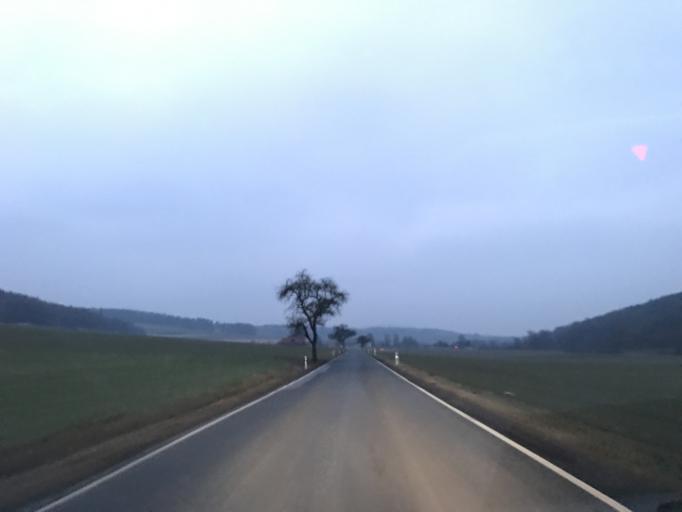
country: DE
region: Hesse
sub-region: Regierungsbezirk Kassel
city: Hofgeismar
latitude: 51.5161
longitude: 9.3871
